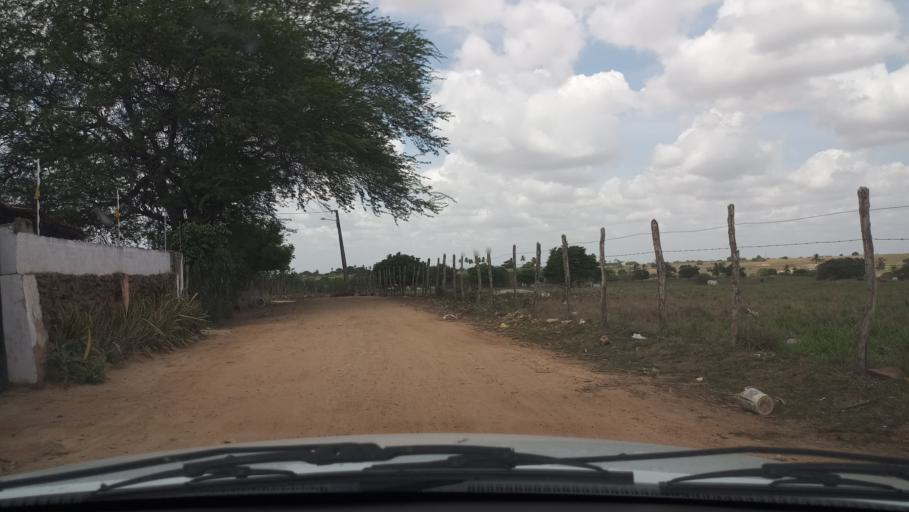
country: BR
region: Rio Grande do Norte
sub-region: Brejinho
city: Brejinho
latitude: -6.2712
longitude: -35.3464
